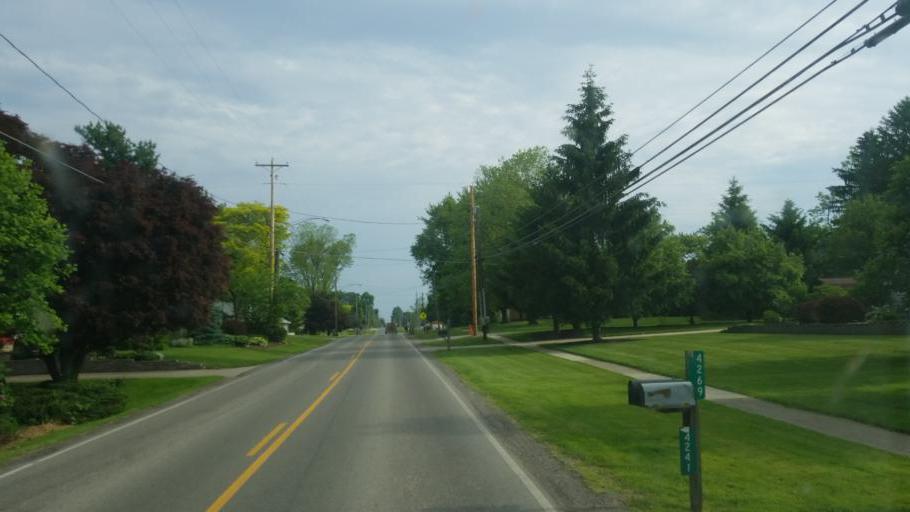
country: US
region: Ohio
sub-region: Wayne County
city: Dalton
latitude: 40.7481
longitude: -81.7451
